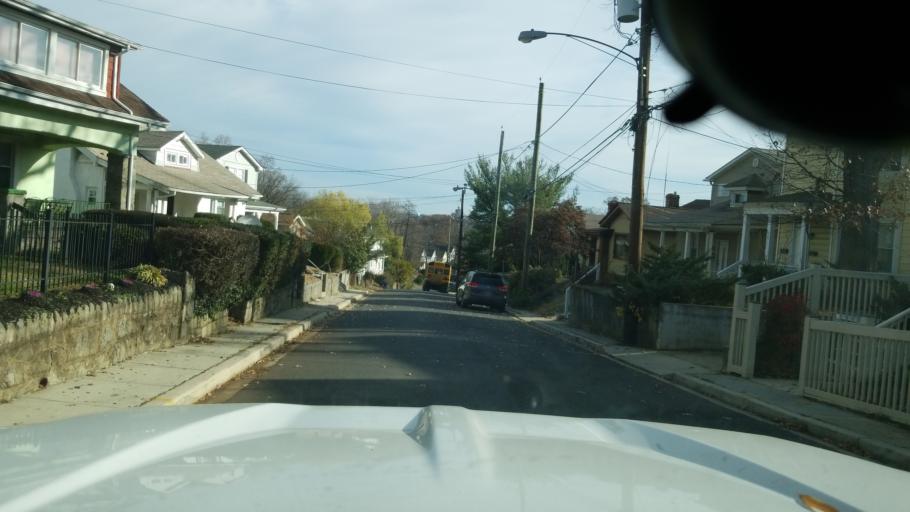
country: US
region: Maryland
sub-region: Prince George's County
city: Mount Rainier
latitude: 38.9324
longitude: -76.9669
